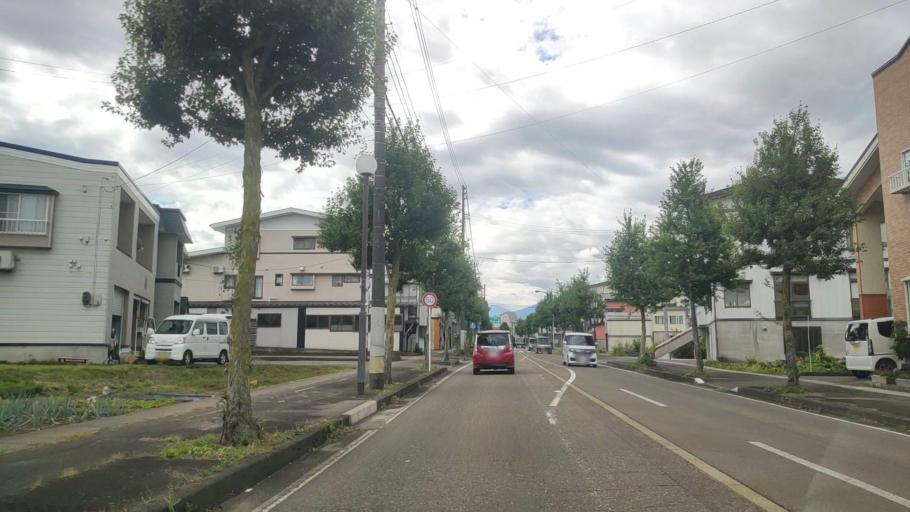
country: JP
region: Niigata
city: Arai
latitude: 37.0275
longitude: 138.2470
